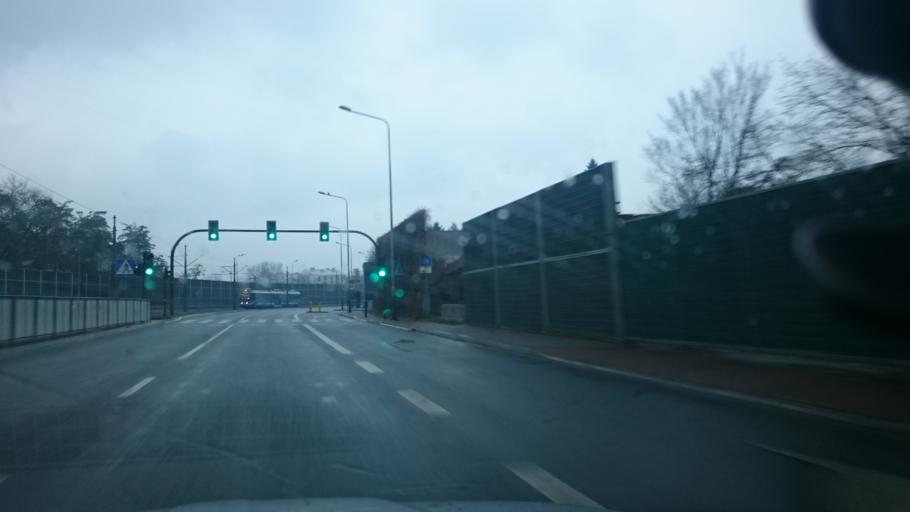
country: PL
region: Lesser Poland Voivodeship
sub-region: Krakow
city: Krakow
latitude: 50.0407
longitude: 19.9784
